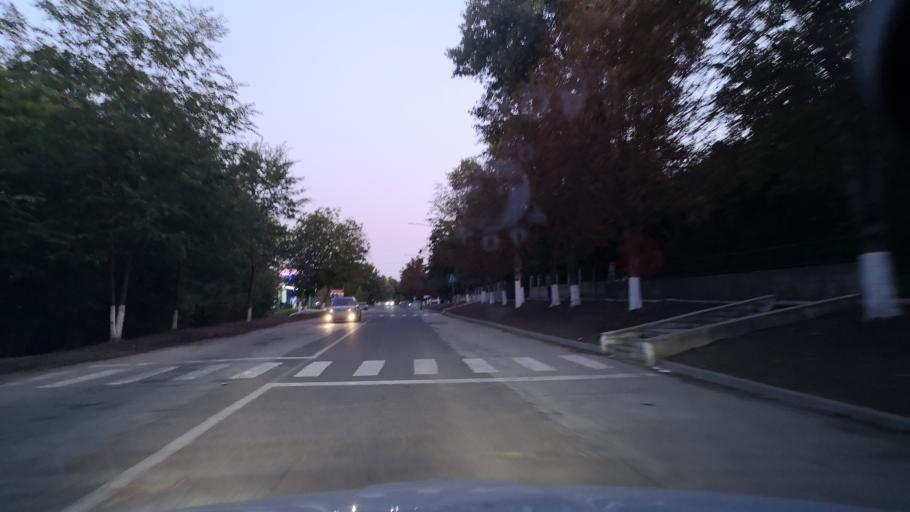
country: MD
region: Orhei
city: Orhei
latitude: 47.3905
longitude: 28.8232
